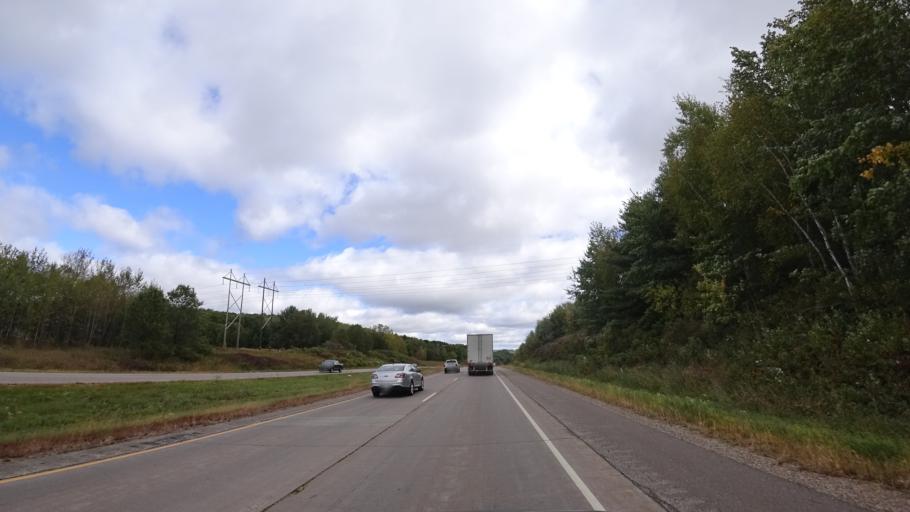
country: US
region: Wisconsin
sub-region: Eau Claire County
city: Eau Claire
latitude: 44.8423
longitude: -91.5209
